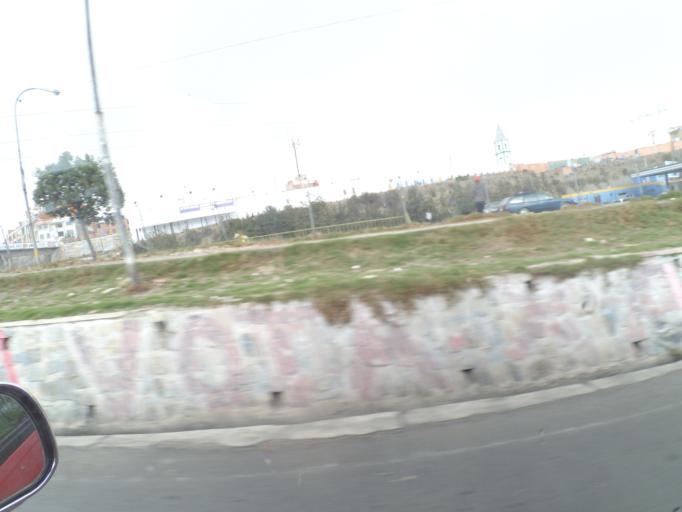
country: BO
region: La Paz
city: La Paz
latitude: -16.5007
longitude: -68.1625
